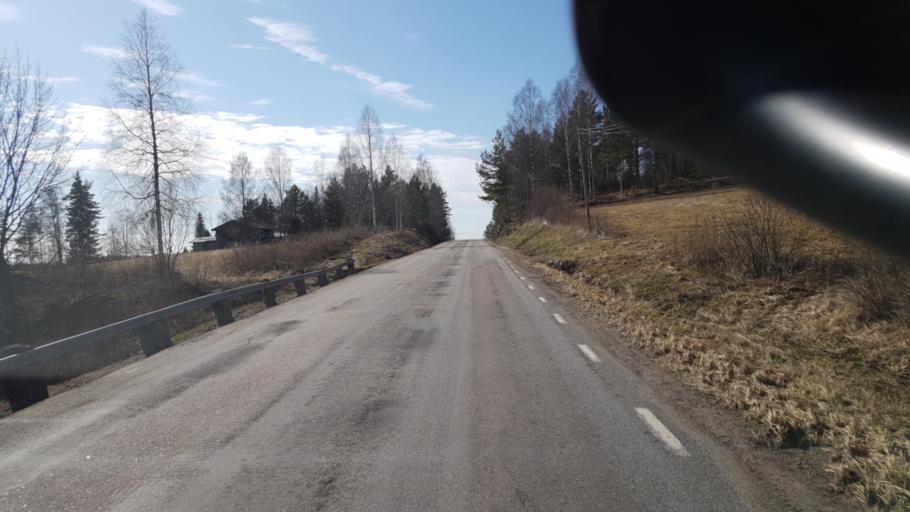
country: SE
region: Vaermland
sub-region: Arvika Kommun
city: Arvika
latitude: 59.6649
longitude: 12.6801
